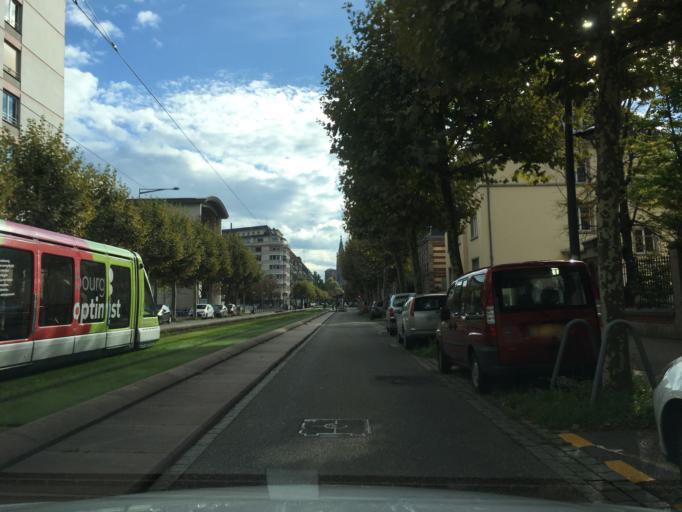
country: FR
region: Alsace
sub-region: Departement du Bas-Rhin
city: Strasbourg
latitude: 48.5914
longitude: 7.7566
